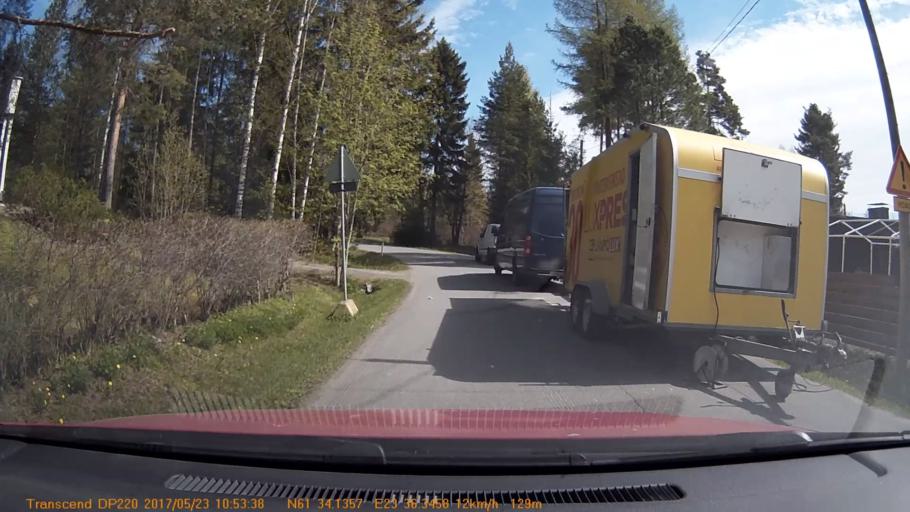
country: FI
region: Pirkanmaa
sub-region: Tampere
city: Yloejaervi
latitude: 61.5690
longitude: 23.6057
